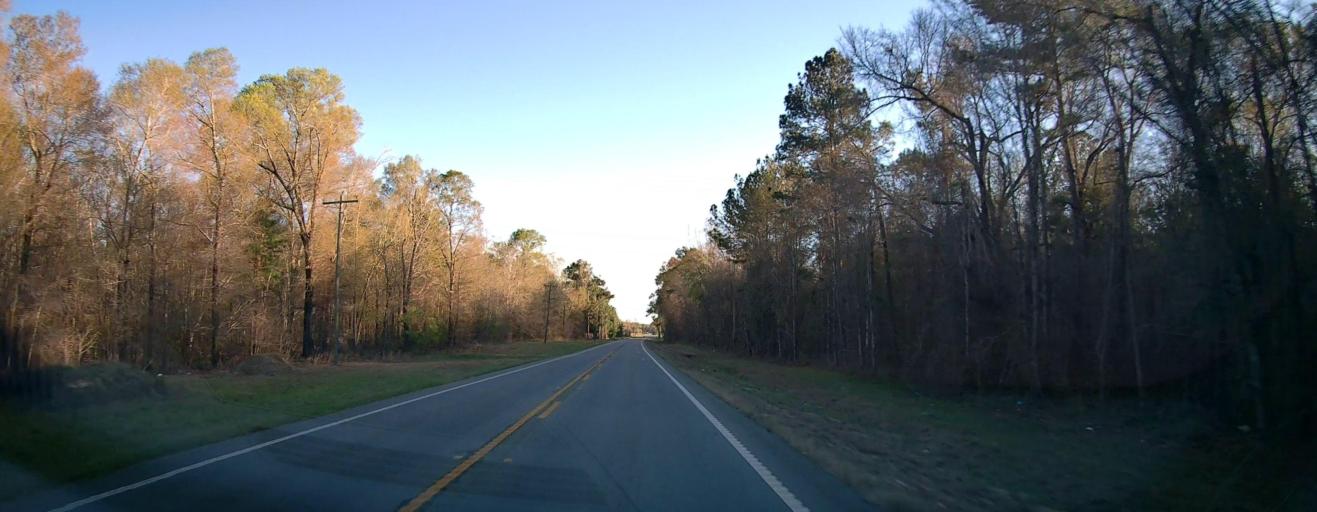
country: US
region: Georgia
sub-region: Wilcox County
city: Abbeville
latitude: 32.0083
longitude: -83.2479
